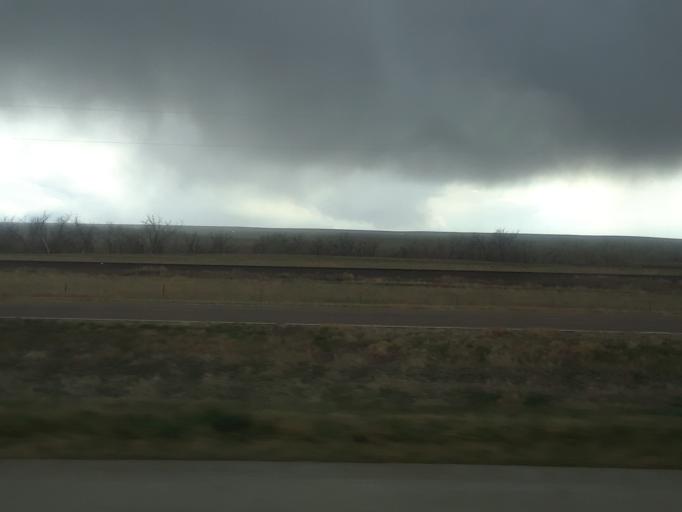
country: US
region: Colorado
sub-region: Arapahoe County
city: Byers
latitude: 39.5361
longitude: -103.9940
